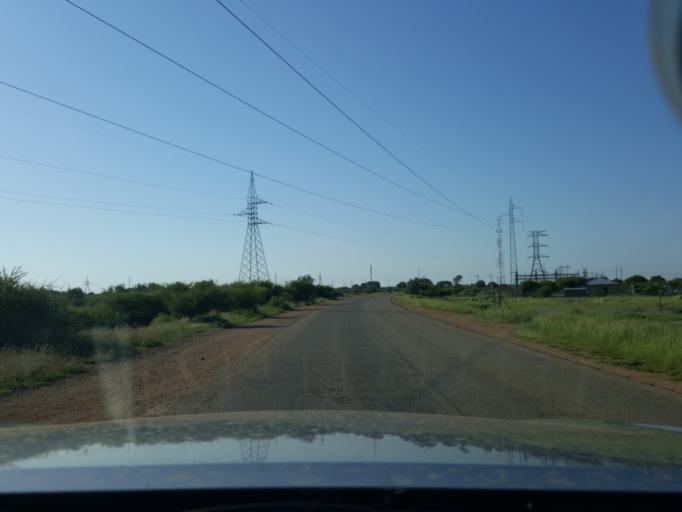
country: ZA
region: North-West
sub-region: Ngaka Modiri Molema District Municipality
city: Mahikeng
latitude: -25.8423
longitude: 25.6757
